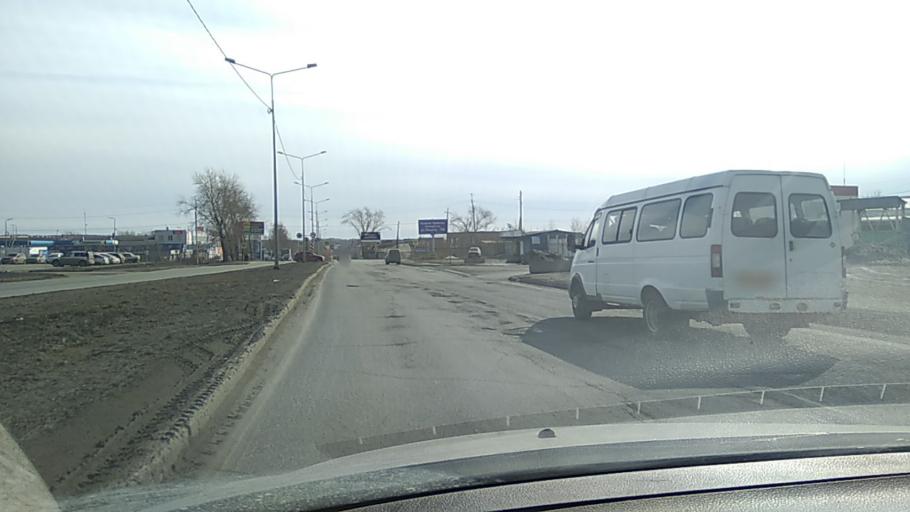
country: RU
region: Sverdlovsk
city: Nizhniy Tagil
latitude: 57.9069
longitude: 60.0090
